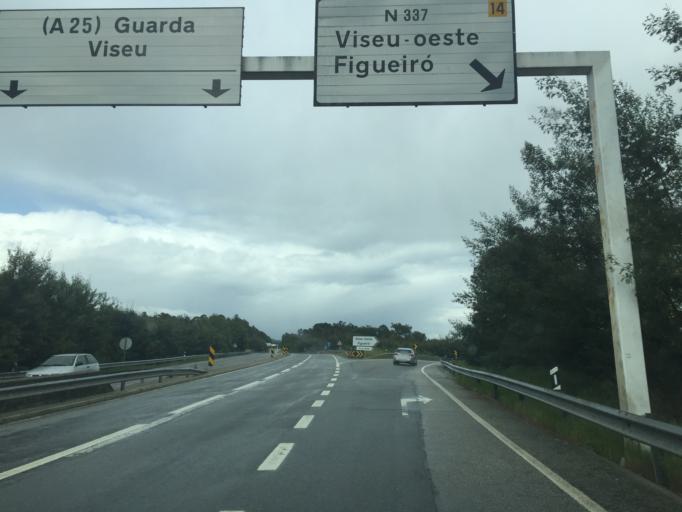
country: PT
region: Viseu
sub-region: Viseu
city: Abraveses
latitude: 40.6676
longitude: -7.9922
